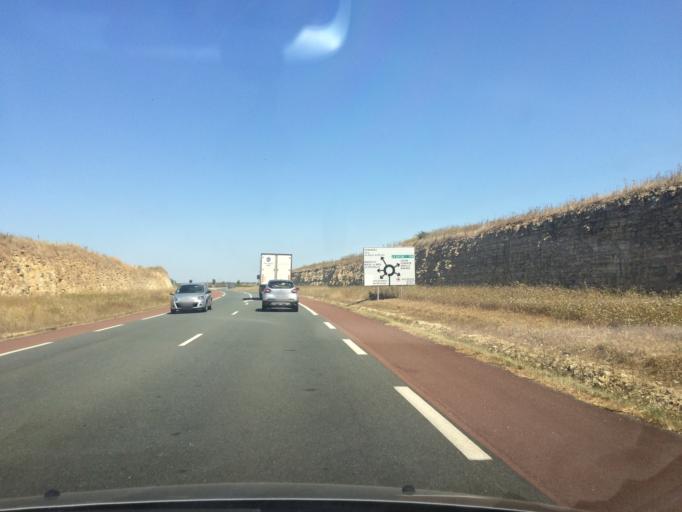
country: FR
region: Poitou-Charentes
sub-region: Departement de la Charente-Maritime
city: Esnandes
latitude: 46.2400
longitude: -1.0782
